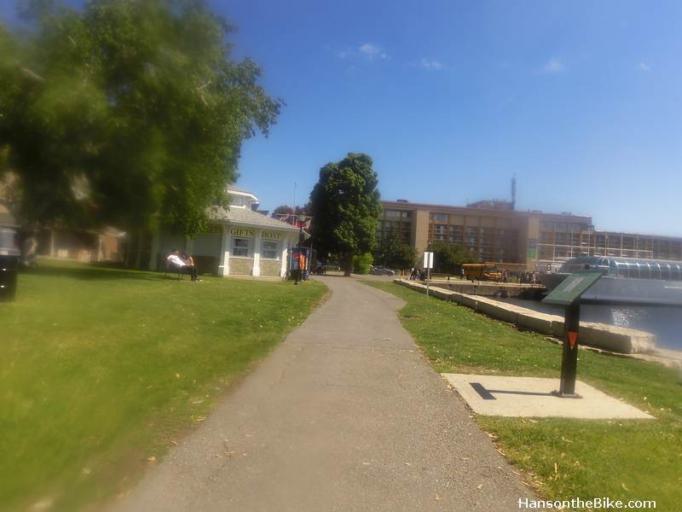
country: CA
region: Ontario
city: Kingston
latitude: 44.2297
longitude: -76.4791
